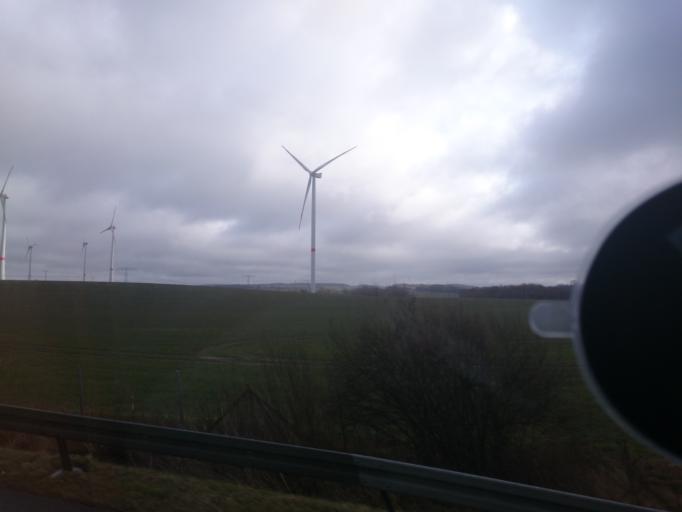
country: DE
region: Mecklenburg-Vorpommern
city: Muhl Rosin
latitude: 53.8214
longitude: 12.3004
